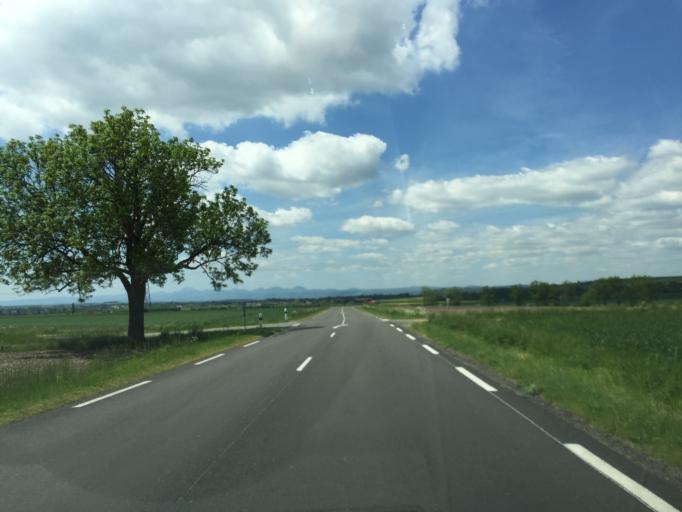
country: FR
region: Auvergne
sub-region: Departement du Puy-de-Dome
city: Randan
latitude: 46.0587
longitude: 3.2838
